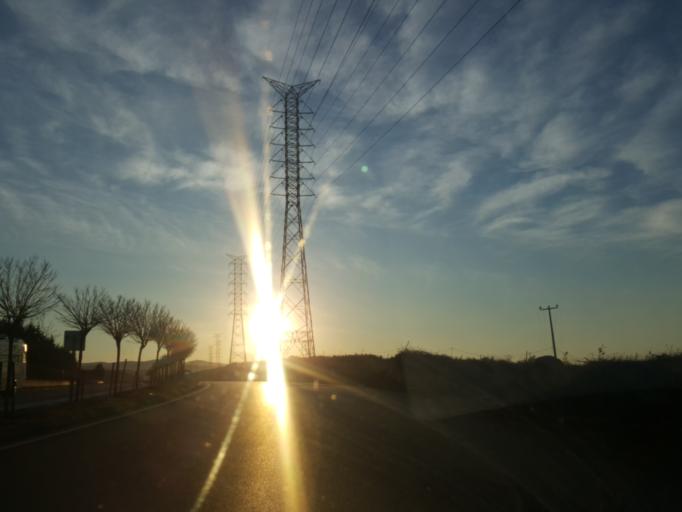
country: TR
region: Kocaeli
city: Tavsancil
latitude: 40.8085
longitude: 29.5621
